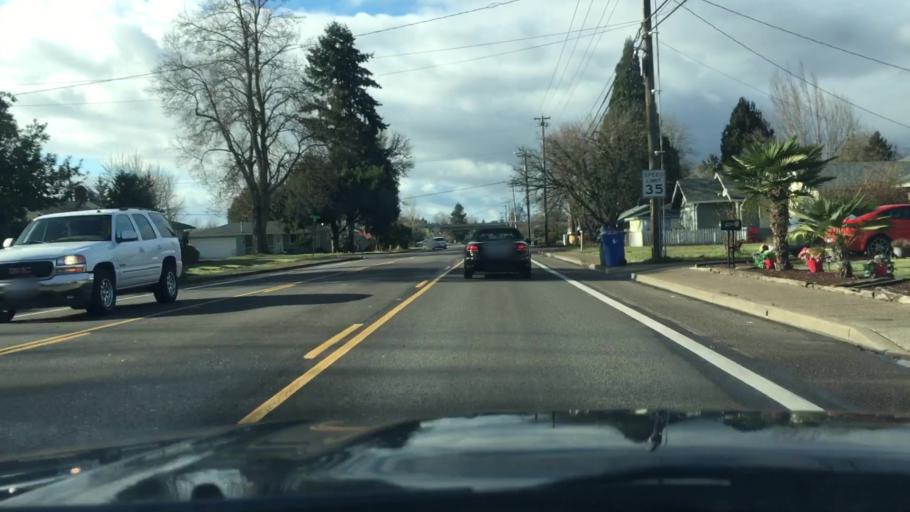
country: US
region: Oregon
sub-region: Lane County
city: Eugene
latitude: 44.0700
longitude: -123.1690
